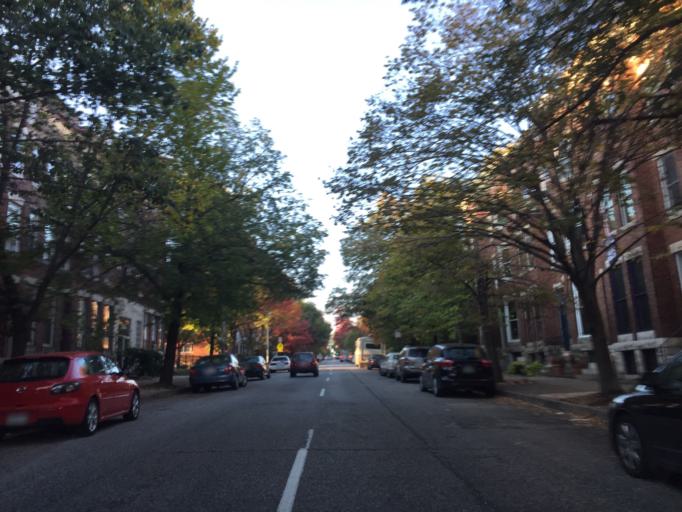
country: US
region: Maryland
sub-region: City of Baltimore
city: Baltimore
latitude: 39.3187
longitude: -76.6143
